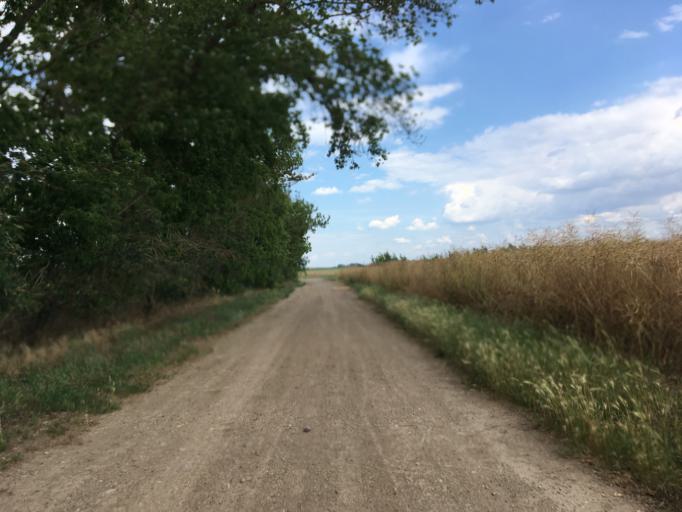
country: DE
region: Saxony-Anhalt
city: Wulfen
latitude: 51.7604
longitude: 11.8951
